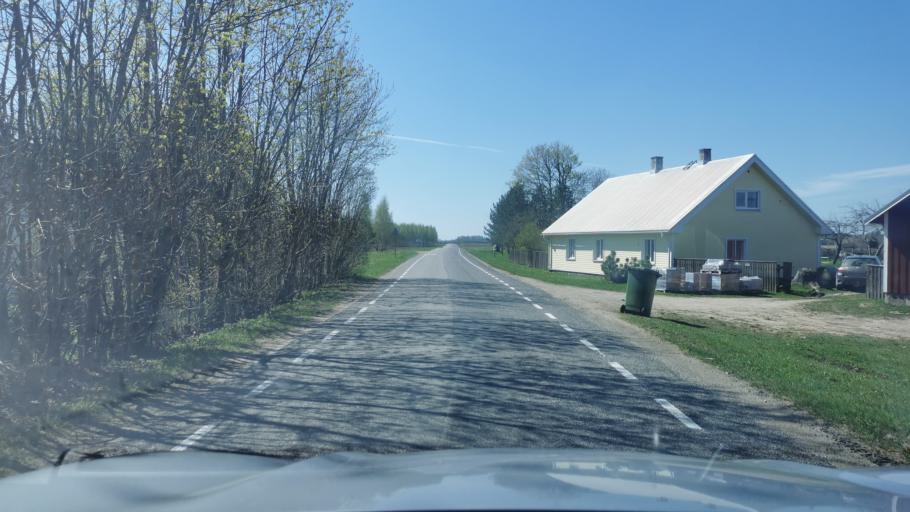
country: EE
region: Laeaene-Virumaa
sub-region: Vinni vald
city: Vinni
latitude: 59.0947
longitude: 26.6156
